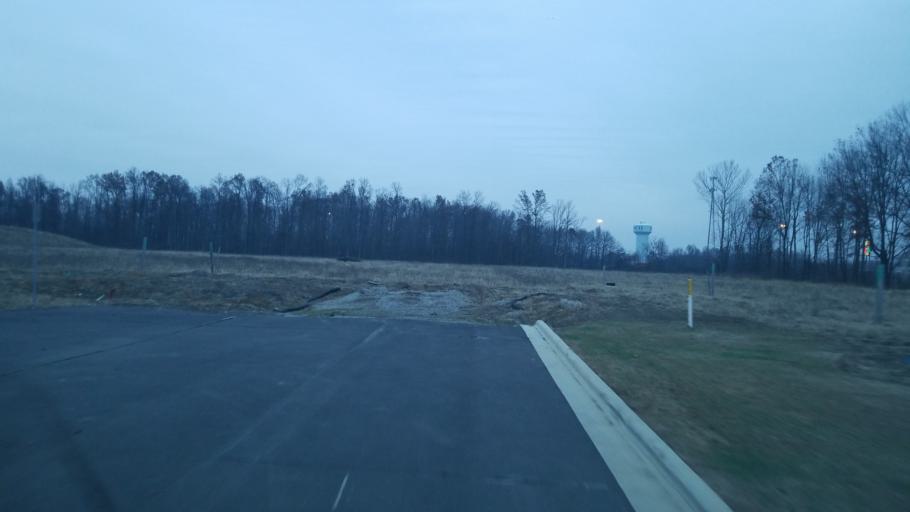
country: US
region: Ohio
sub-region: Delaware County
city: Sunbury
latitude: 40.2719
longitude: -82.9322
